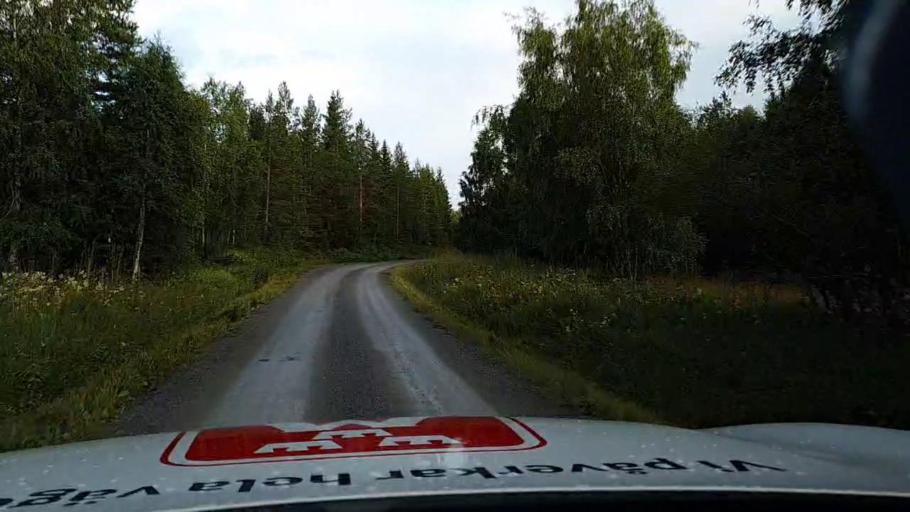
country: SE
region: Jaemtland
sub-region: Bergs Kommun
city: Hoverberg
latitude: 62.8650
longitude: 14.5285
